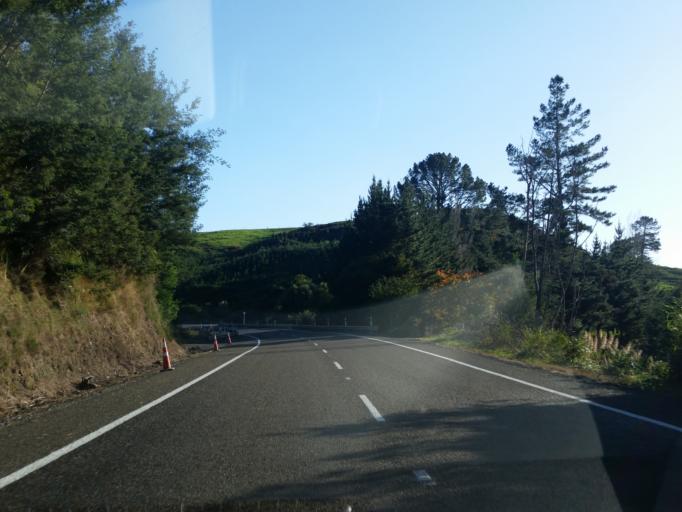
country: NZ
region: Bay of Plenty
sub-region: Western Bay of Plenty District
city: Waihi Beach
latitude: -37.4539
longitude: 175.8930
